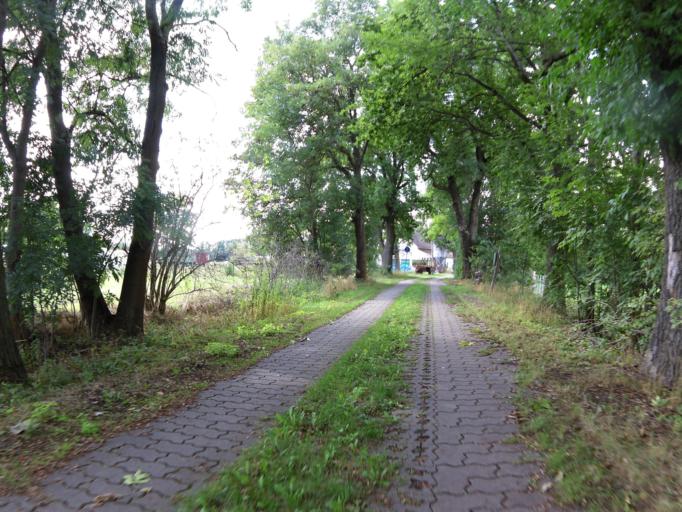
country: DE
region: Brandenburg
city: Storkow
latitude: 52.2361
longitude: 13.8733
